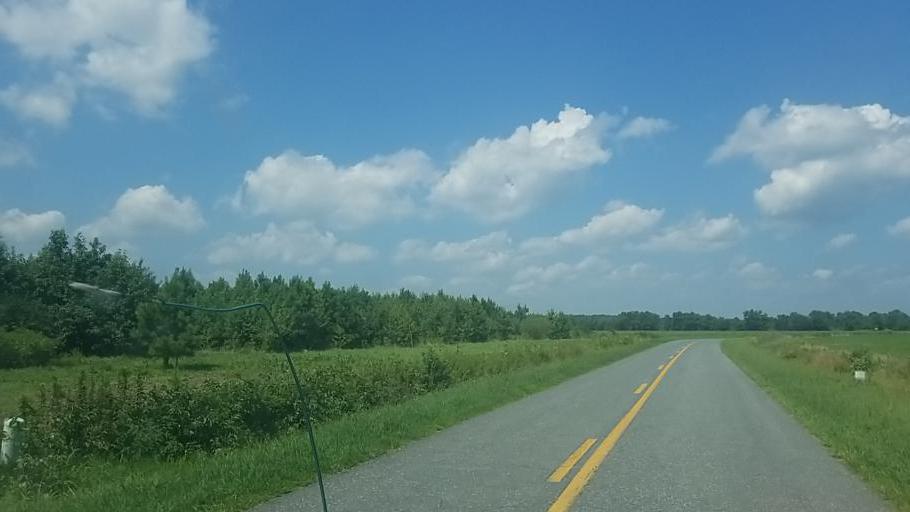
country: US
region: Maryland
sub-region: Dorchester County
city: Hurlock
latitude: 38.4776
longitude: -75.8375
